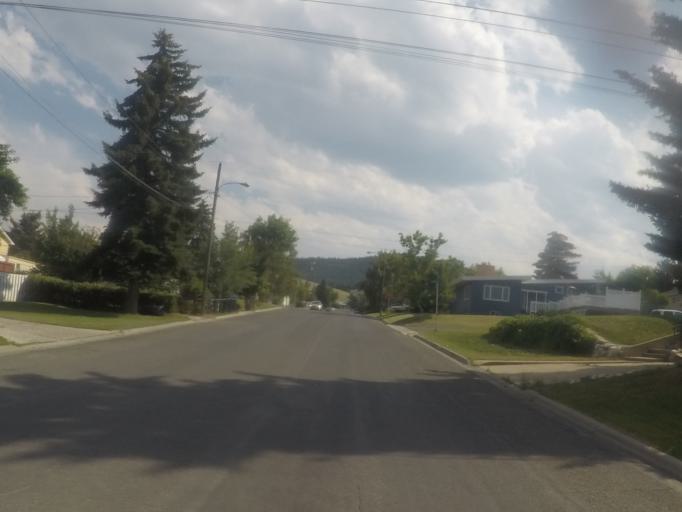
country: US
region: Montana
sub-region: Lewis and Clark County
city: Helena
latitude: 46.5849
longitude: -112.0072
